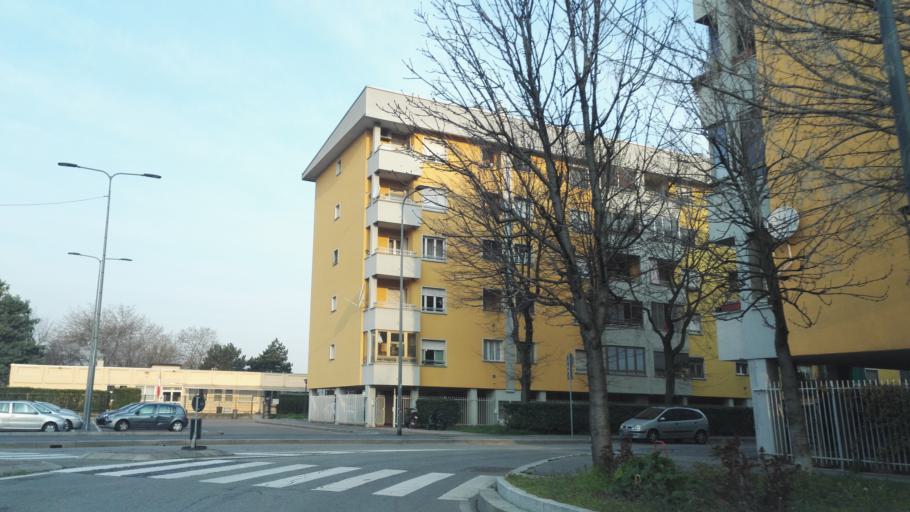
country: IT
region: Lombardy
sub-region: Citta metropolitana di Milano
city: Linate
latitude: 45.4395
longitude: 9.2643
